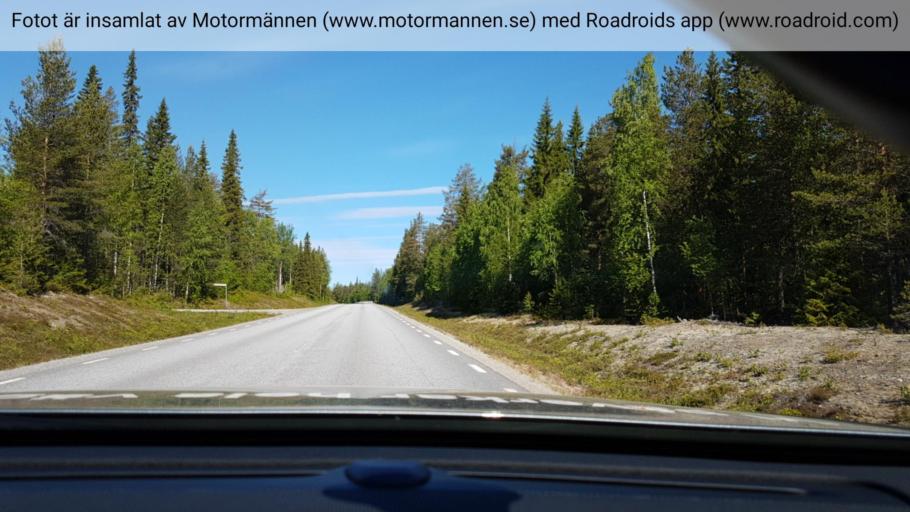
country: SE
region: Vaesterbotten
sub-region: Lycksele Kommun
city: Lycksele
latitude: 64.0284
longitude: 18.6357
